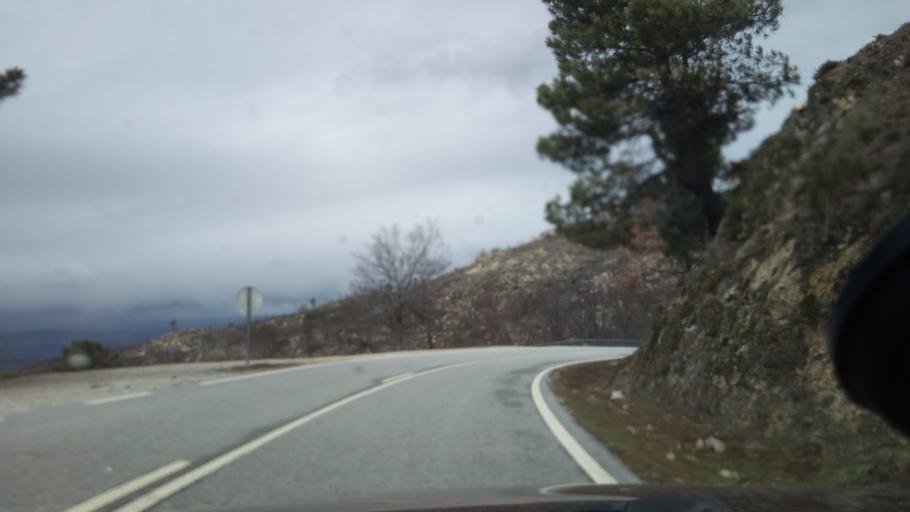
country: PT
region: Guarda
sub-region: Manteigas
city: Manteigas
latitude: 40.4602
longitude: -7.5879
